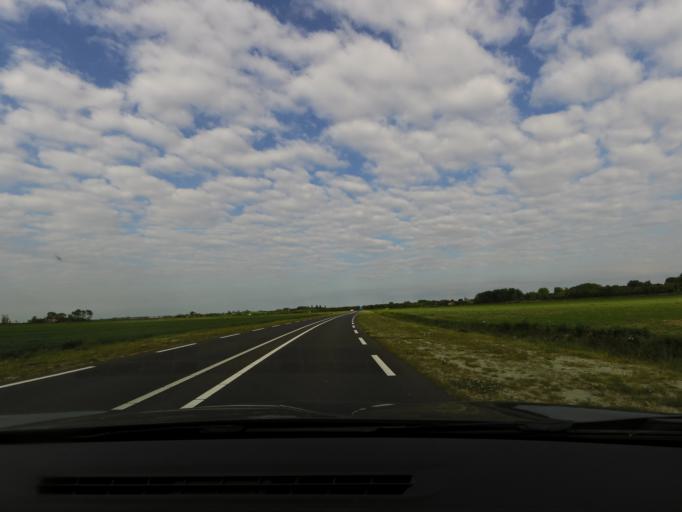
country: NL
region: Zeeland
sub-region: Schouwen-Duiveland
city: Renesse
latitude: 51.7299
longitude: 3.7957
